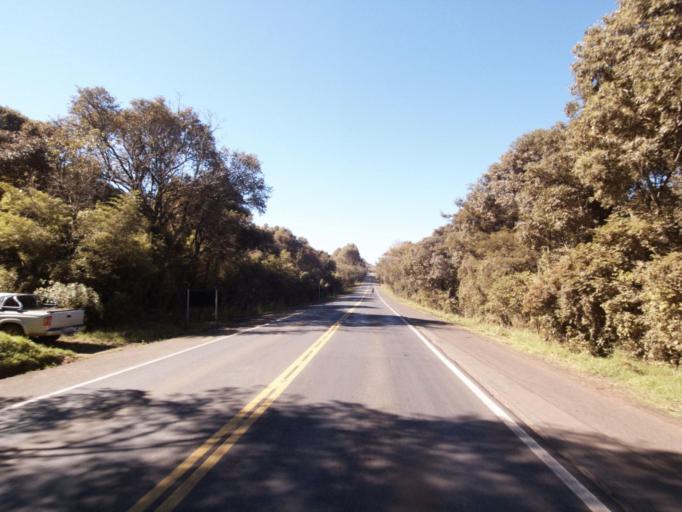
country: BR
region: Santa Catarina
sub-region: Chapeco
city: Chapeco
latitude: -26.9373
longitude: -52.8047
